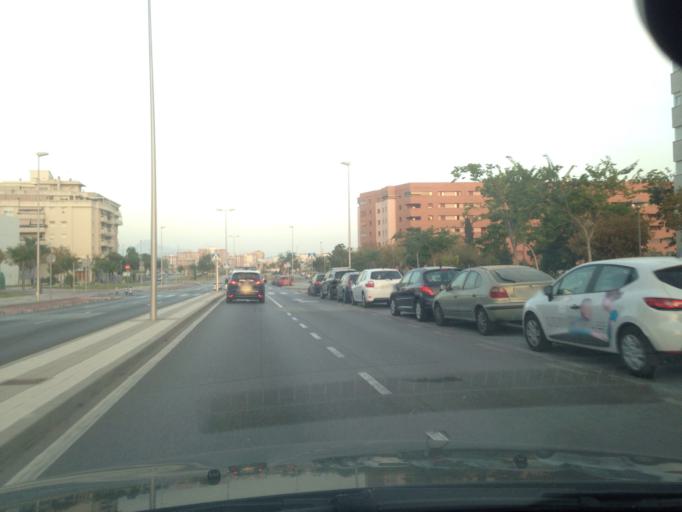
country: ES
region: Andalusia
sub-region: Provincia de Malaga
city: Malaga
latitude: 36.7182
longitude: -4.4625
